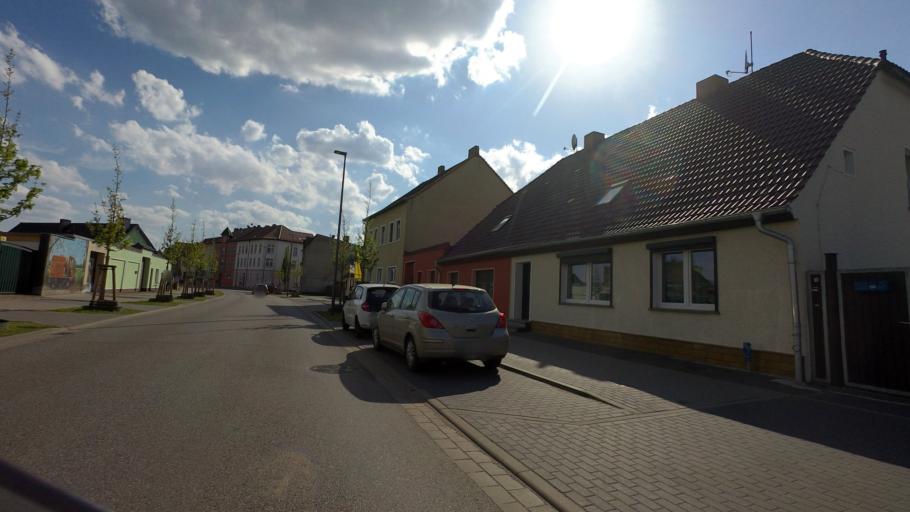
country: DE
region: Brandenburg
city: Zehdenick
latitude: 52.9886
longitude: 13.3407
